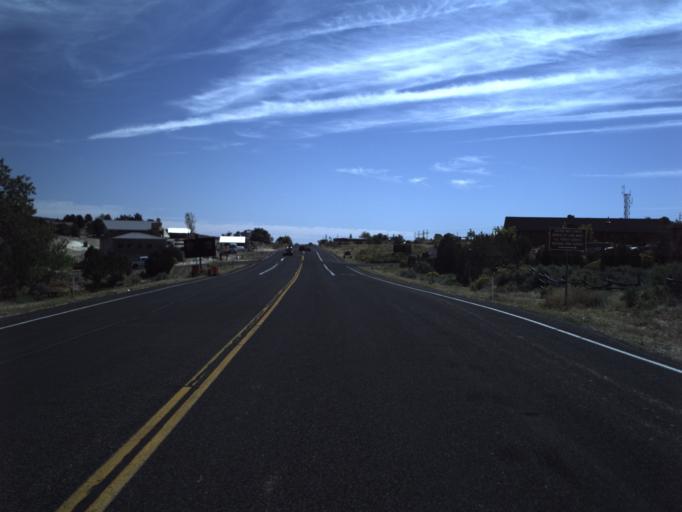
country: US
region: Utah
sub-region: Wayne County
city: Loa
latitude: 37.7743
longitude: -111.6165
